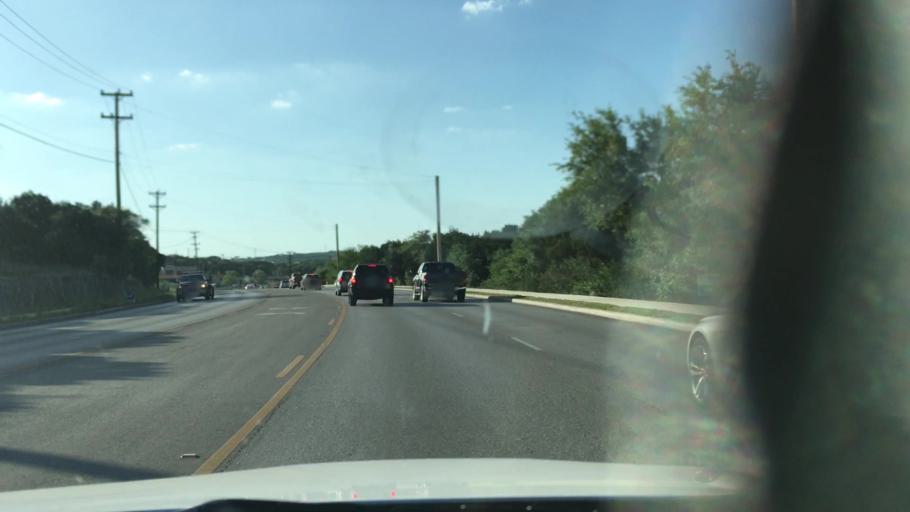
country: US
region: Texas
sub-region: Bexar County
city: Timberwood Park
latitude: 29.6591
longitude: -98.4333
